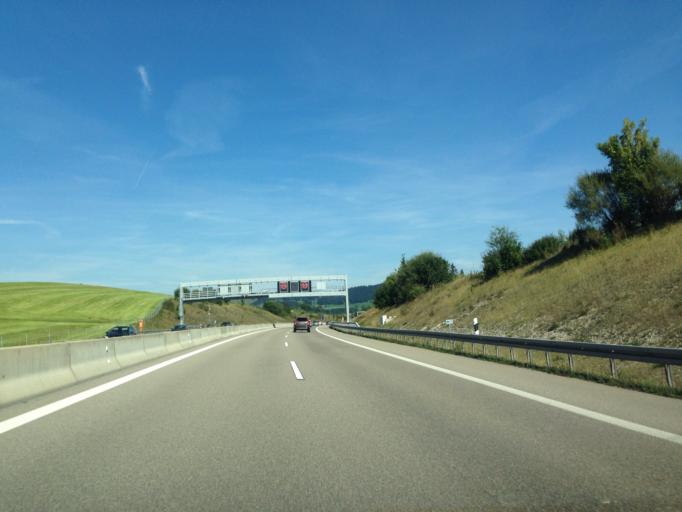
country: DE
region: Bavaria
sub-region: Swabia
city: Hopferau
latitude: 47.5924
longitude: 10.6565
